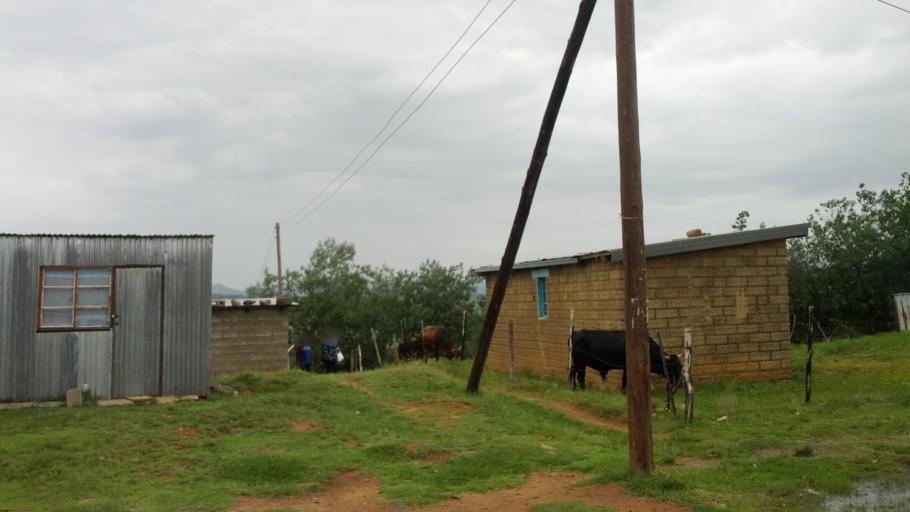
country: LS
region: Berea
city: Teyateyaneng
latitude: -29.1088
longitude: 27.9649
